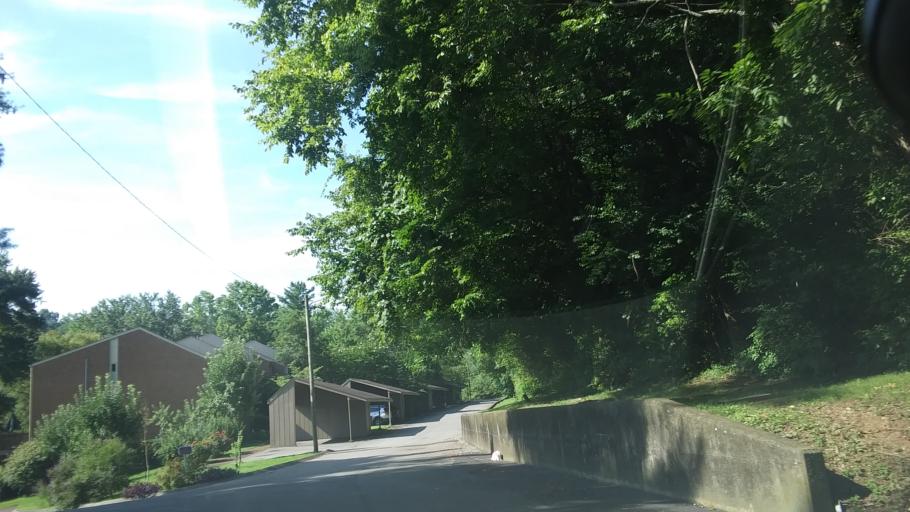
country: US
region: Tennessee
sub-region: Davidson County
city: Belle Meade
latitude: 36.0781
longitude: -86.8894
